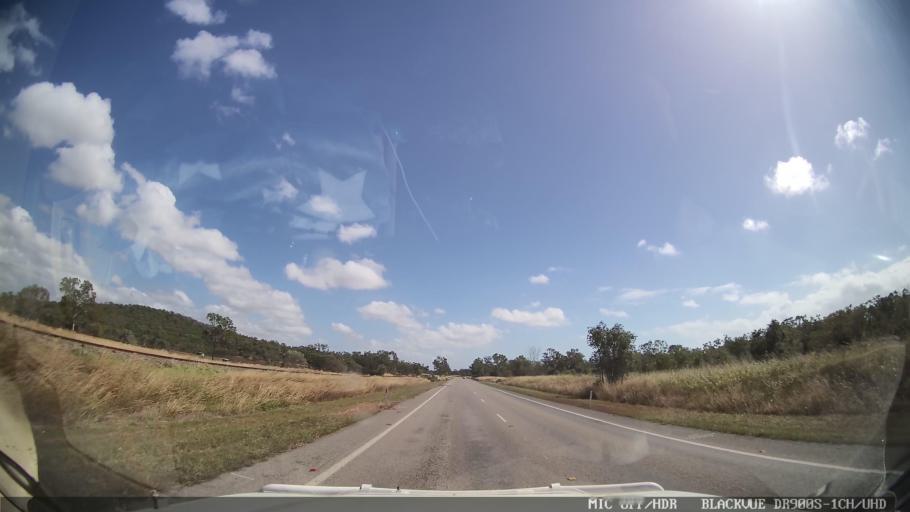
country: AU
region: Queensland
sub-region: Whitsunday
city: Bowen
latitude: -20.1816
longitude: 148.3516
